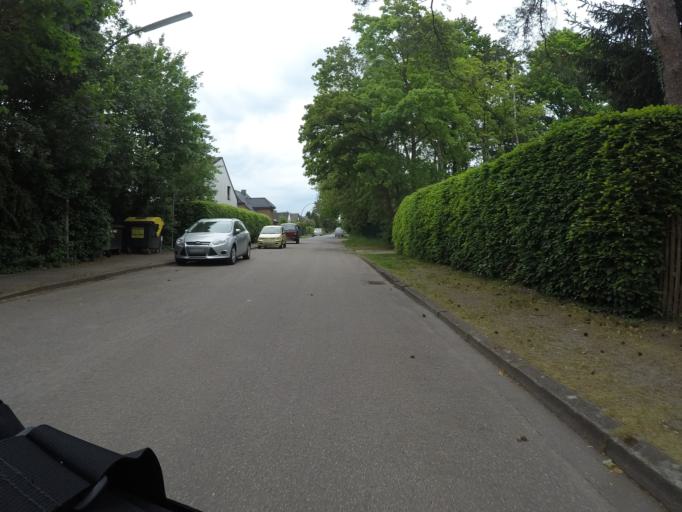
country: DE
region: Hamburg
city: Langenhorn
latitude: 53.6394
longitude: 9.9811
